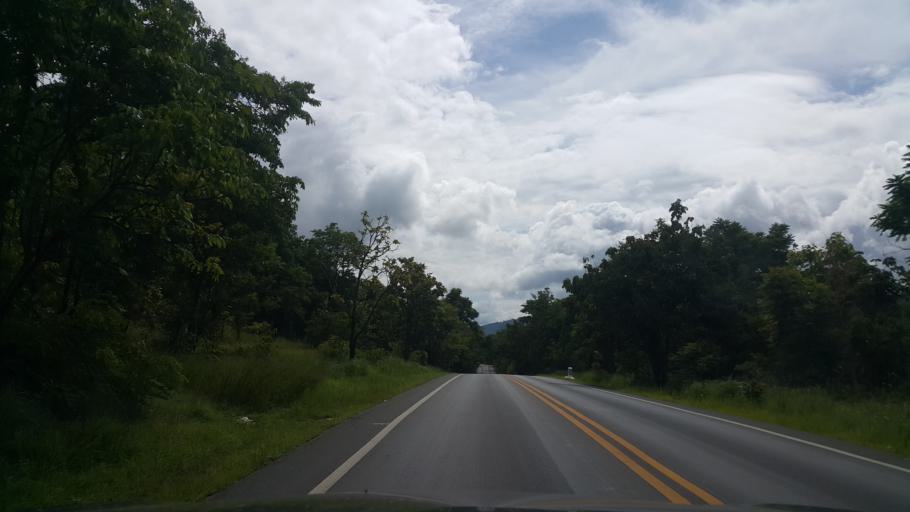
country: TH
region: Uttaradit
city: Thong Saen Khan
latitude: 17.3814
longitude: 100.2835
